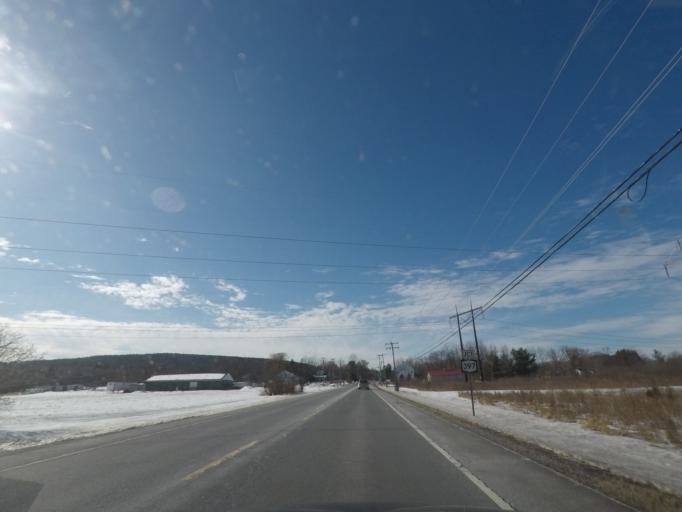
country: US
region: New York
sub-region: Albany County
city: Altamont
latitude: 42.7392
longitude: -74.0118
